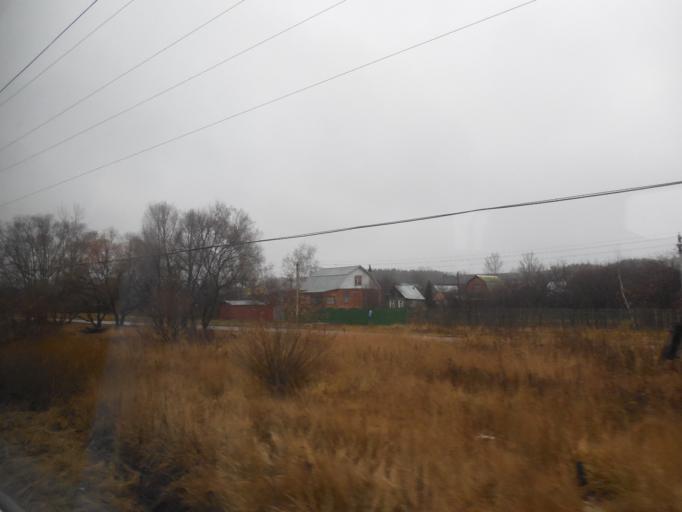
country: RU
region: Moskovskaya
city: Belyye Stolby
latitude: 55.3261
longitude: 37.8572
